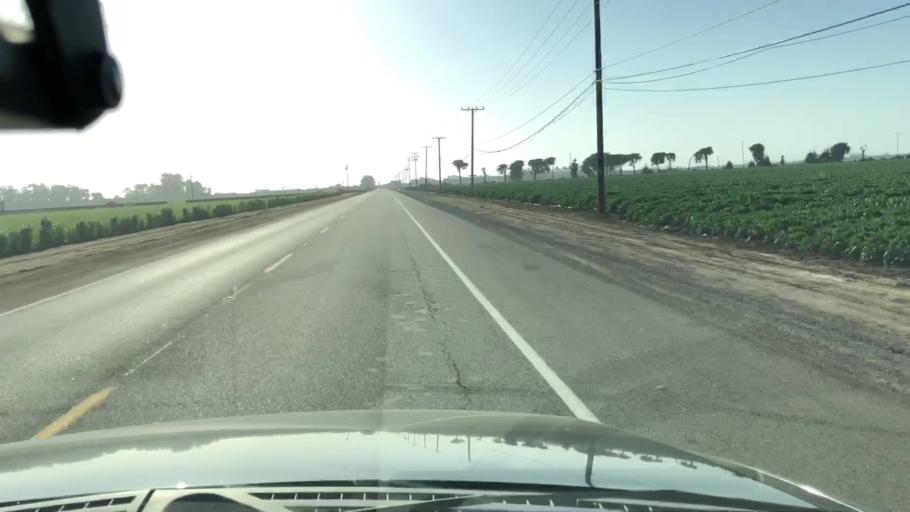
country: US
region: California
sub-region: Ventura County
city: Oxnard Shores
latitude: 34.2196
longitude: -119.2346
